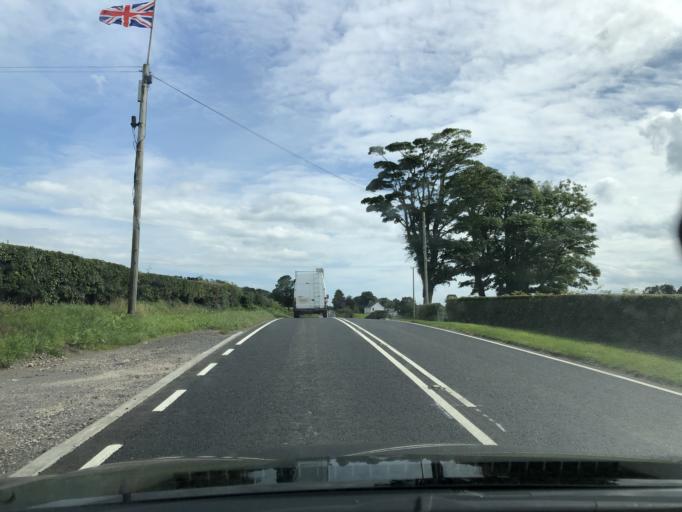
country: GB
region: Northern Ireland
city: Annahilt
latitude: 54.4398
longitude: -5.9403
